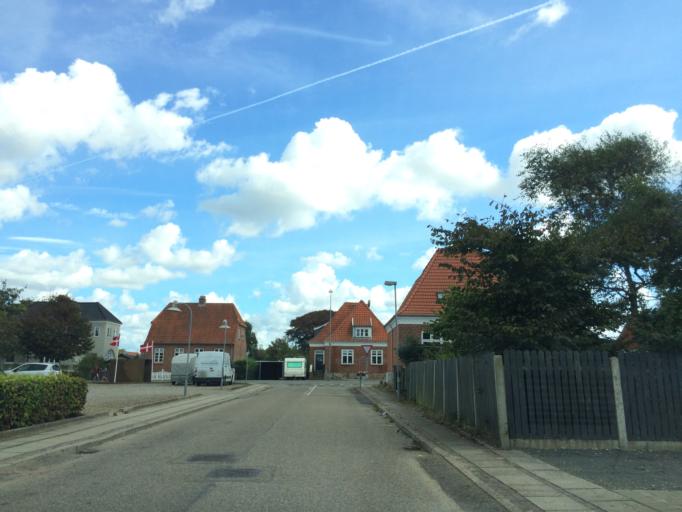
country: DK
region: Central Jutland
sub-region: Holstebro Kommune
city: Ulfborg
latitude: 56.2706
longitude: 8.3192
